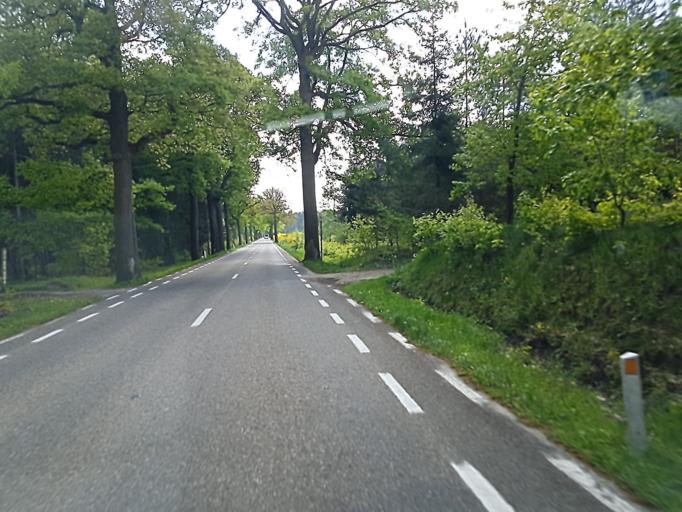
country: BE
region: Flanders
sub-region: Provincie Antwerpen
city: Laakdal
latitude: 51.0457
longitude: 5.0050
